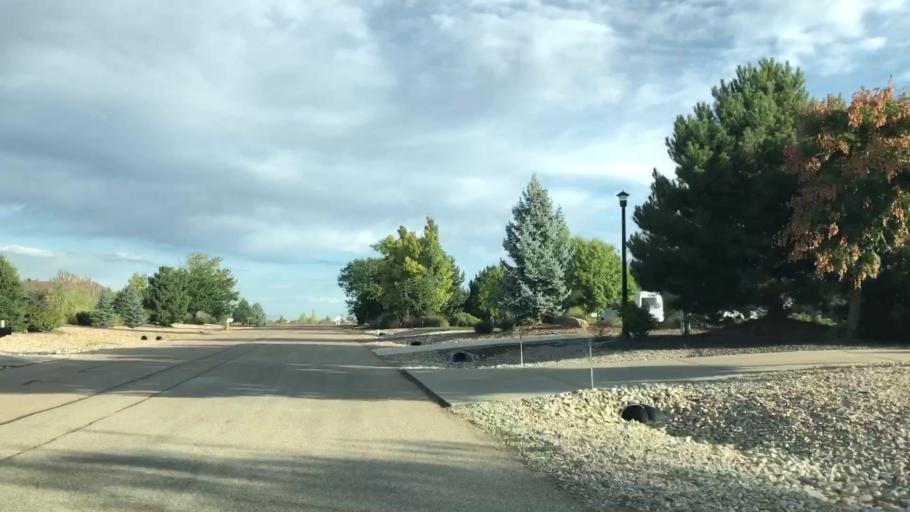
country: US
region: Colorado
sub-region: Weld County
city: Windsor
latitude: 40.4422
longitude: -104.9526
